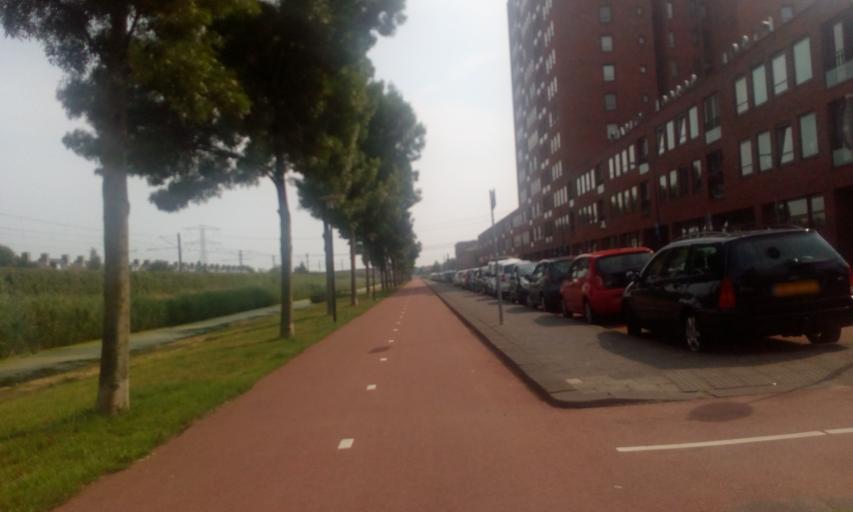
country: NL
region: South Holland
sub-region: Gemeente Capelle aan den IJssel
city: Capelle aan den IJssel
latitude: 51.9691
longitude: 4.5799
